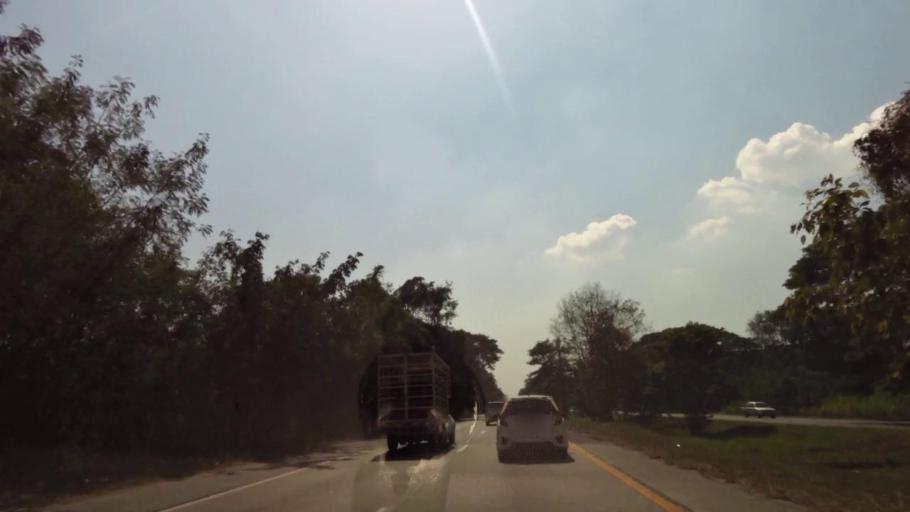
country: TH
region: Phichit
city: Wachira Barami
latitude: 16.5546
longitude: 100.1472
